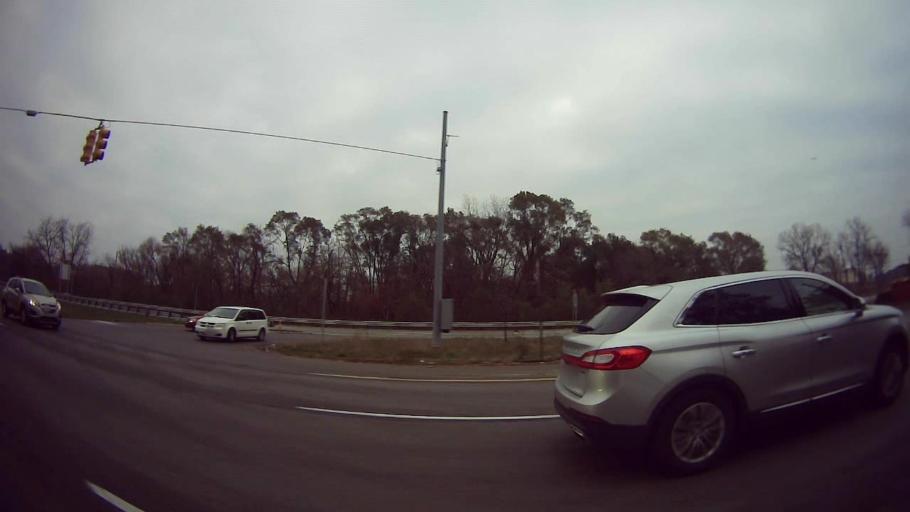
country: US
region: Michigan
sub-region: Wayne County
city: Dearborn Heights
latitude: 42.3432
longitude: -83.2738
